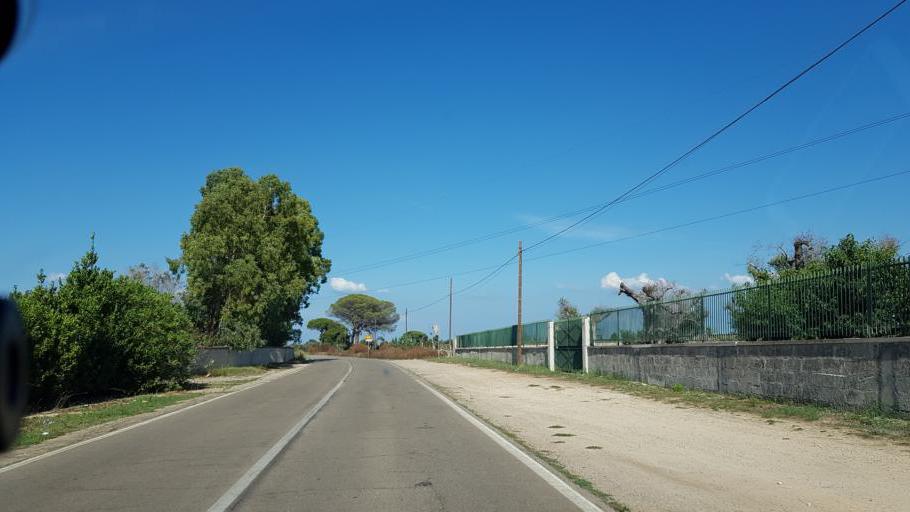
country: IT
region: Apulia
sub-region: Provincia di Lecce
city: Monteroni di Lecce
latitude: 40.2937
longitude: 18.0940
